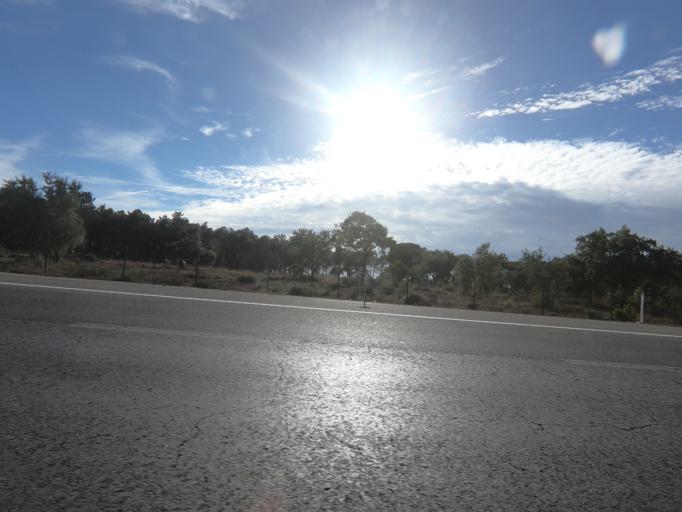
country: PT
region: Setubal
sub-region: Barreiro
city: Santo Antonio da Charneca
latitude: 38.6198
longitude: -9.0337
